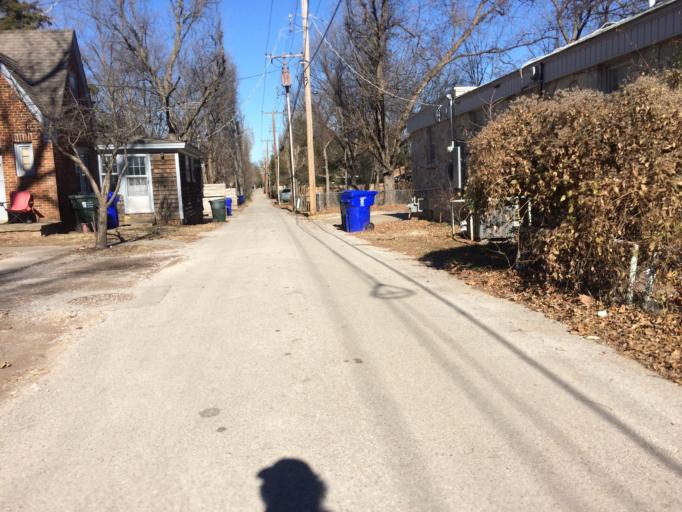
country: US
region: Oklahoma
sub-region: Cleveland County
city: Norman
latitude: 35.2039
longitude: -97.4523
